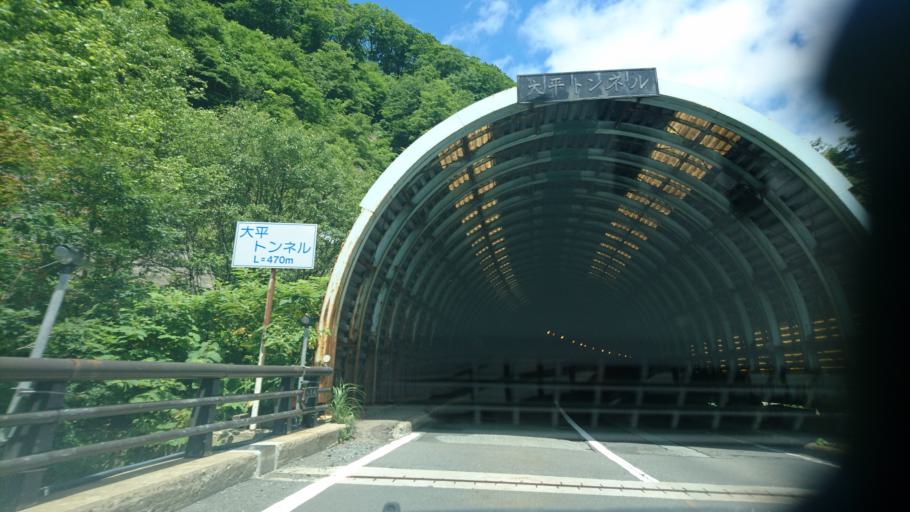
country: JP
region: Iwate
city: Shizukuishi
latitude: 39.6913
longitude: 140.7966
